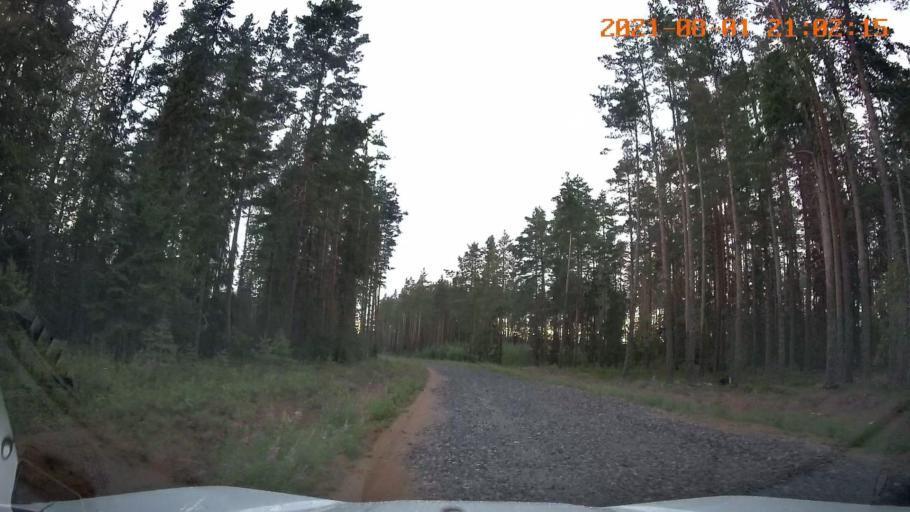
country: RU
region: Leningrad
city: Syas'stroy
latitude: 60.4875
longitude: 32.6672
